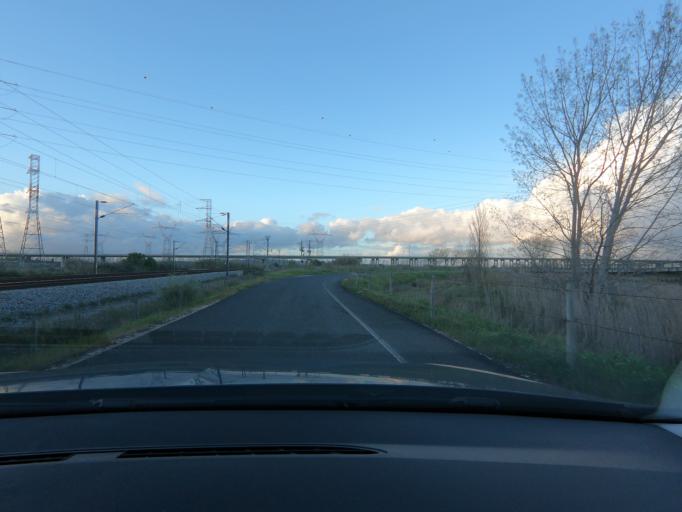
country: PT
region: Lisbon
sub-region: Alenquer
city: Carregado
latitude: 39.0120
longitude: -8.9488
